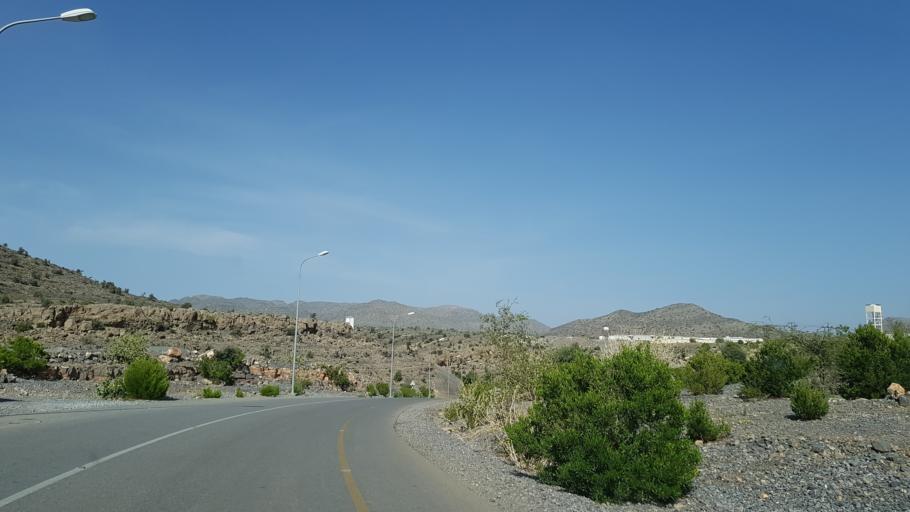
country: OM
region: Muhafazat ad Dakhiliyah
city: Izki
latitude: 23.0905
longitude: 57.6887
